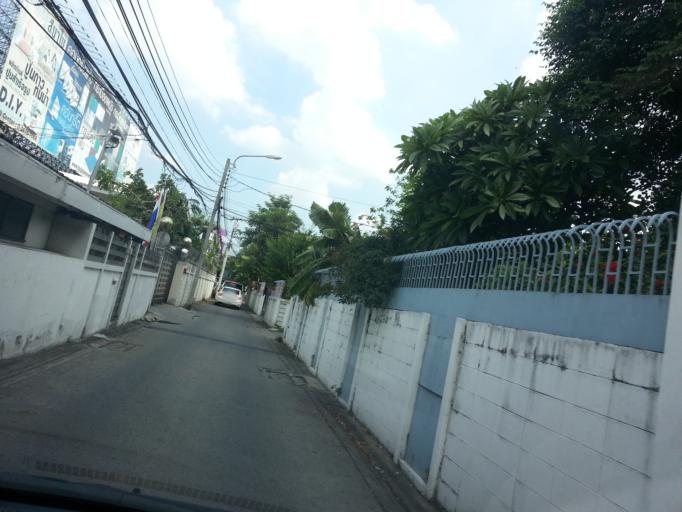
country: TH
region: Bangkok
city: Khlong Toei
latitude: 13.7136
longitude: 100.5772
